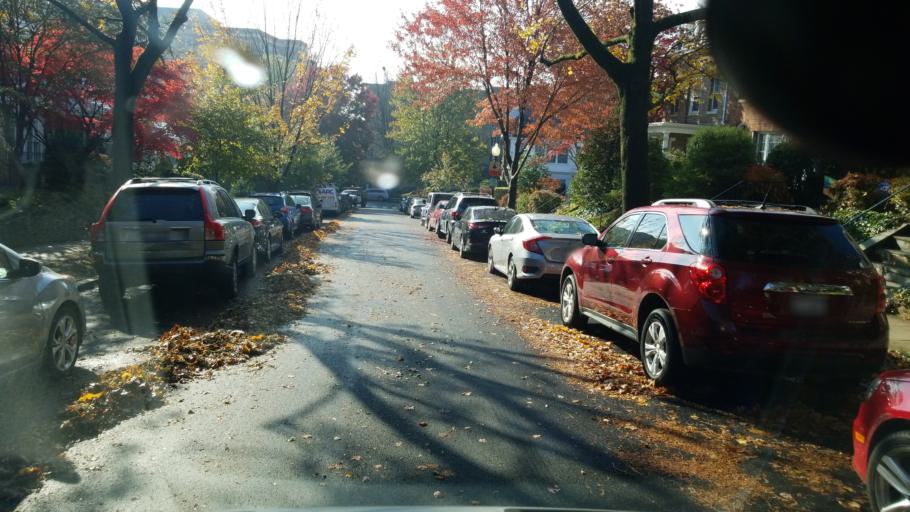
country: US
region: Washington, D.C.
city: Washington, D.C.
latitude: 38.9269
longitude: -77.0564
